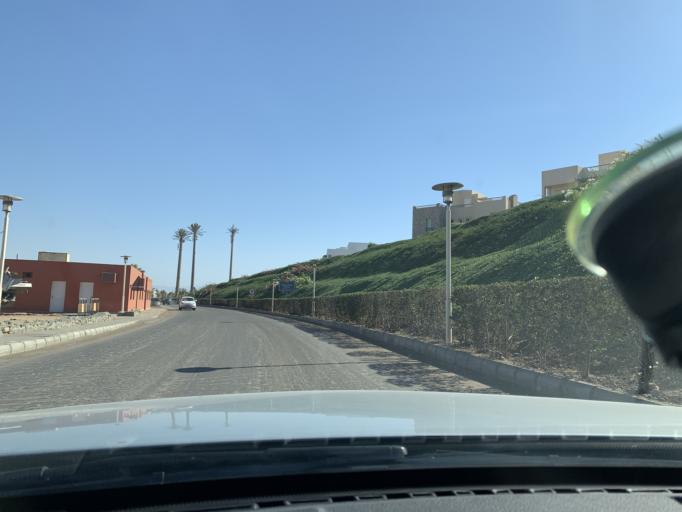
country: EG
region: Red Sea
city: El Gouna
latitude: 27.4085
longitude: 33.6730
